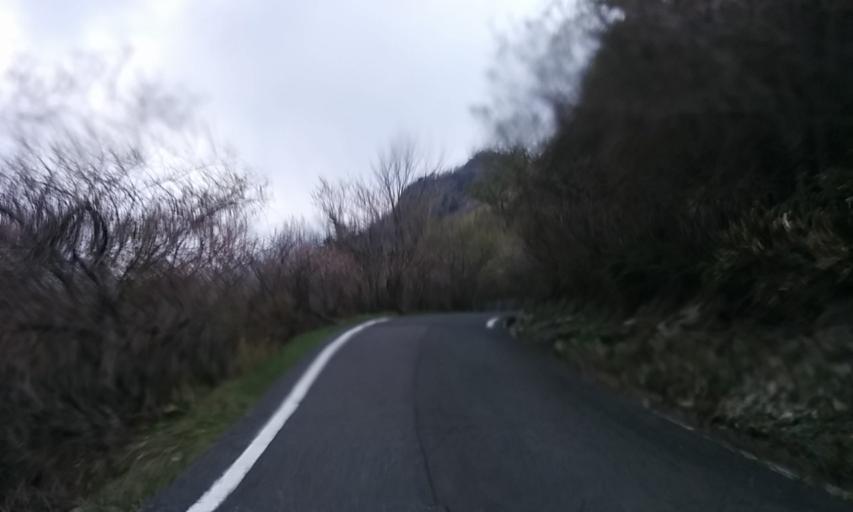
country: JP
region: Ehime
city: Saijo
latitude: 33.7794
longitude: 133.2188
